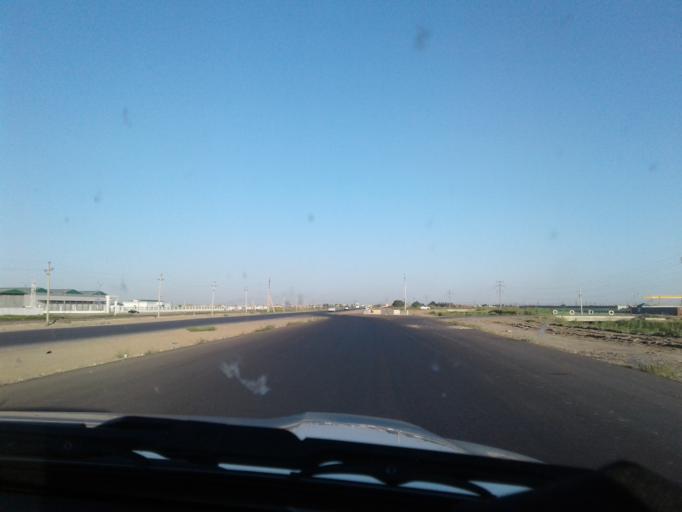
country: TM
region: Mary
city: Mary
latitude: 37.5749
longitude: 61.8007
